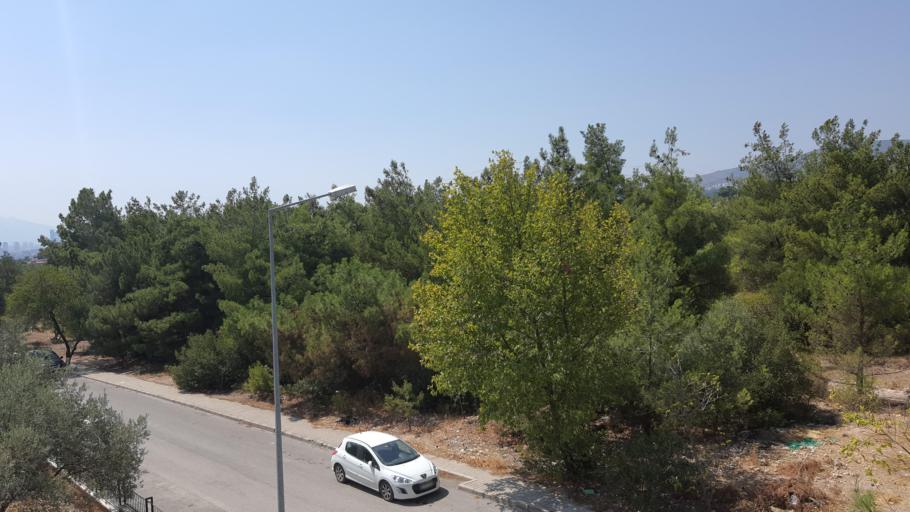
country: TR
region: Izmir
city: Bornova
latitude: 38.4754
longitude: 27.2548
